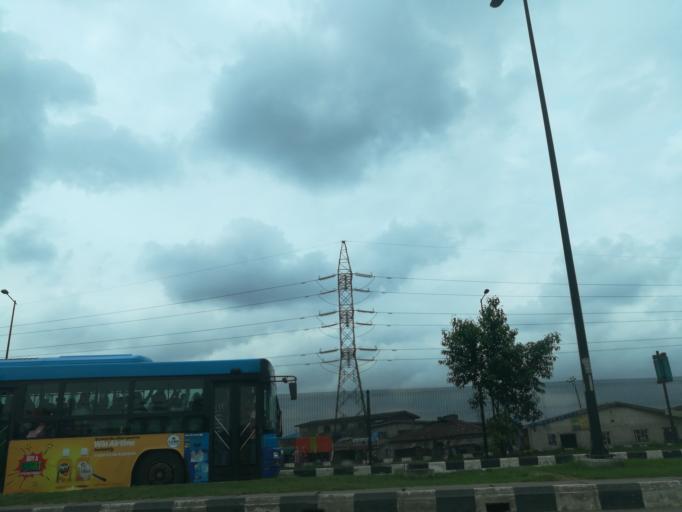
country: NG
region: Lagos
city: Ojota
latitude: 6.6044
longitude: 3.4023
